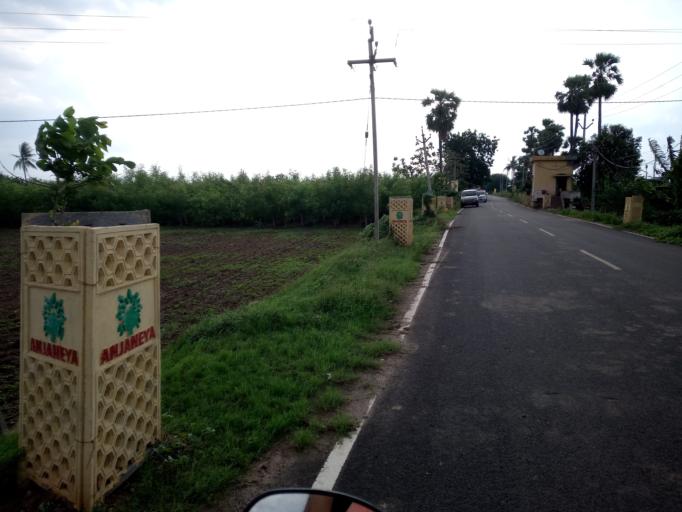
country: IN
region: Andhra Pradesh
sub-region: Guntur
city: Tadepalle
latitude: 16.5027
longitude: 80.5818
